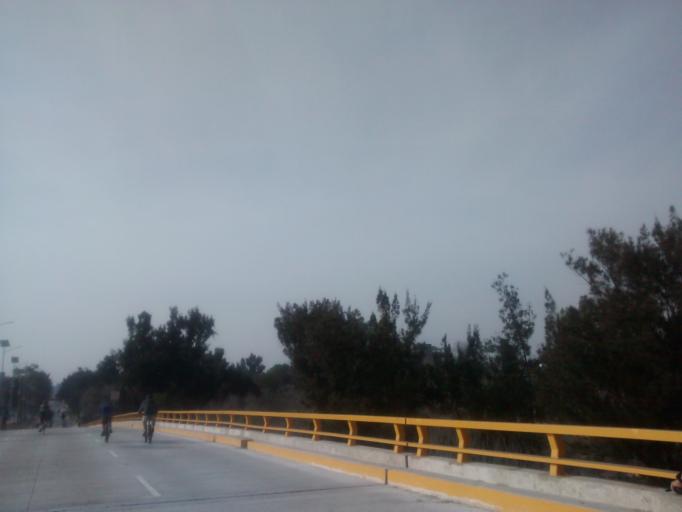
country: MX
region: Mexico City
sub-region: Iztacalco
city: Iztacalco
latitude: 19.3958
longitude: -99.0991
